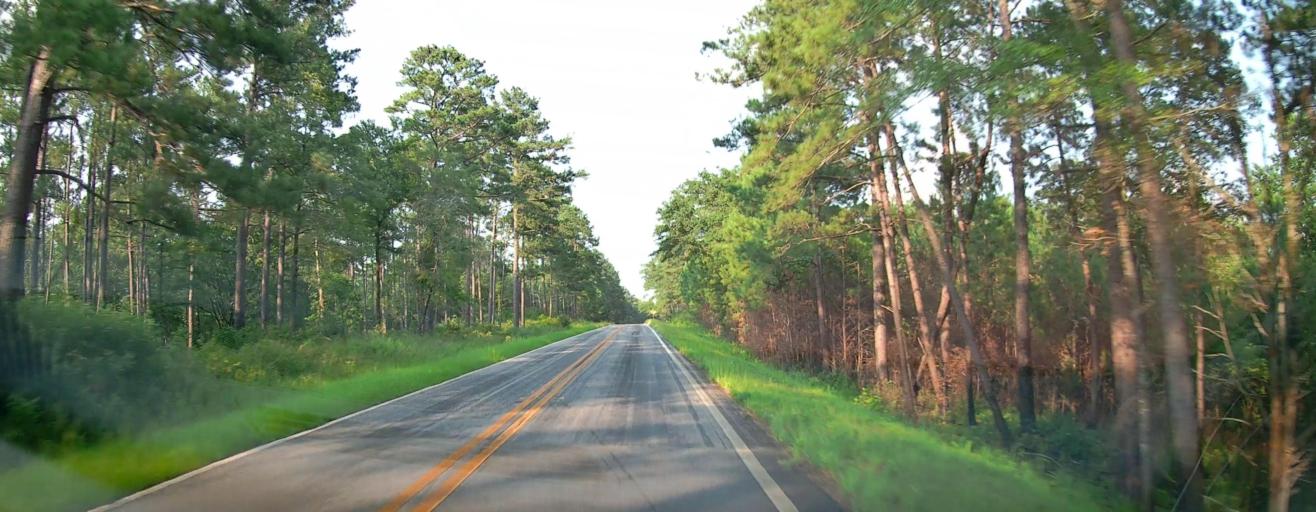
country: US
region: Georgia
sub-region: Jasper County
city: Monticello
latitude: 33.0982
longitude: -83.7304
